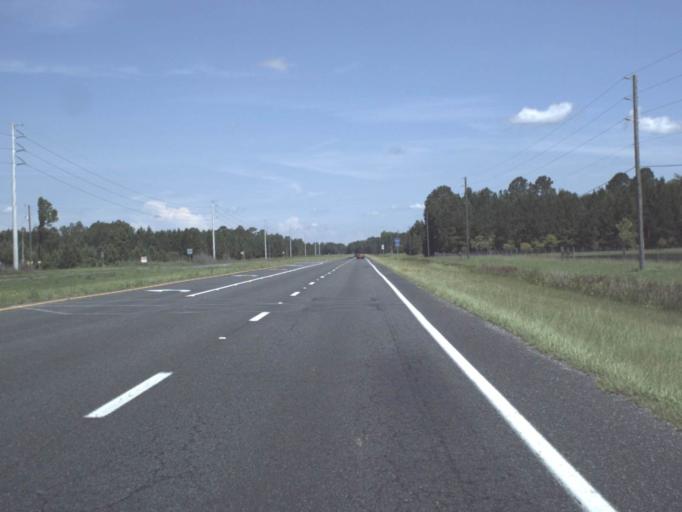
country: US
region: Florida
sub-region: Levy County
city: Bronson
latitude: 29.4679
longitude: -82.6706
